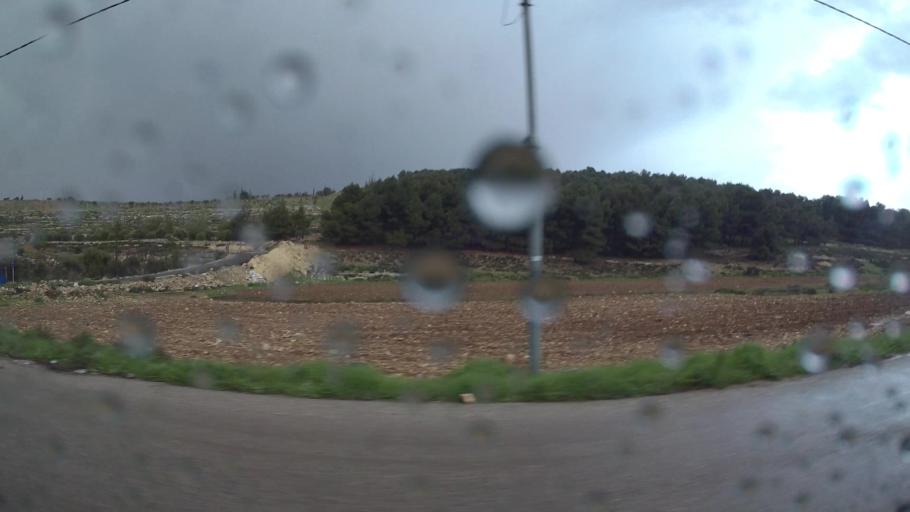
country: JO
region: Amman
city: Umm as Summaq
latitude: 31.8681
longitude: 35.8642
